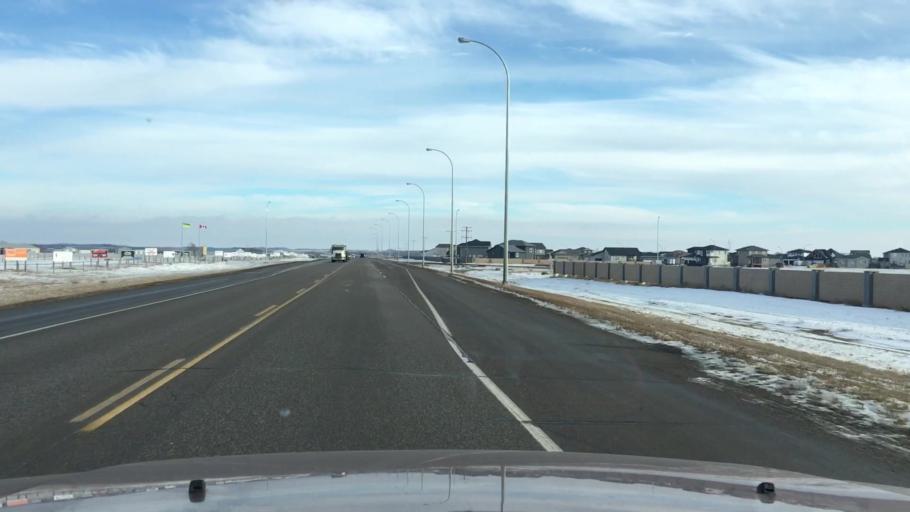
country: CA
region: Saskatchewan
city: Pilot Butte
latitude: 50.4871
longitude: -104.4229
